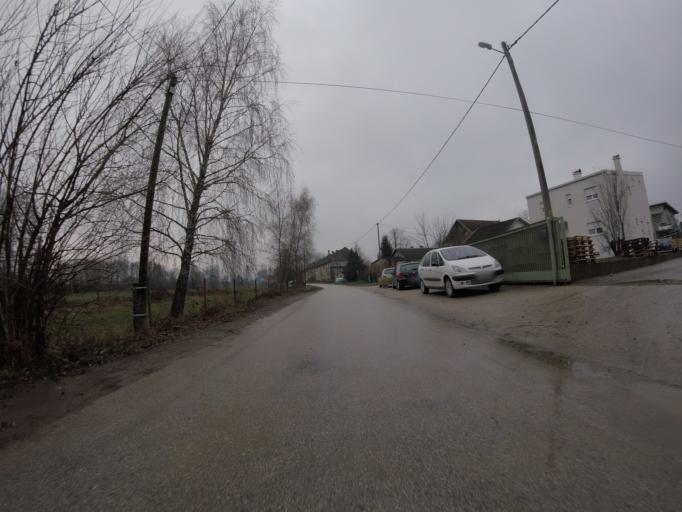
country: HR
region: Zagrebacka
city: Kuce
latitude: 45.7053
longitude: 16.1259
